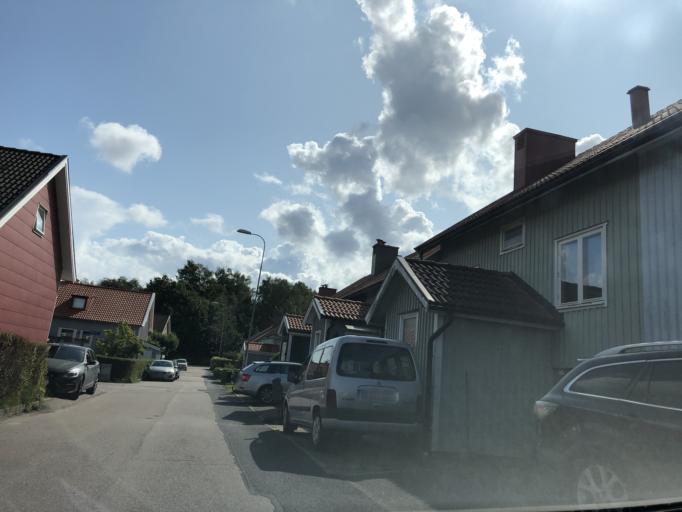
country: SE
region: Vaestra Goetaland
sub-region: Goteborg
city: Majorna
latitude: 57.7180
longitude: 11.9017
